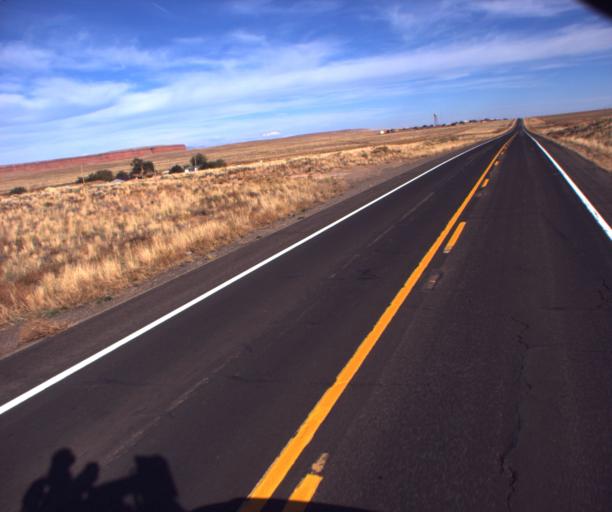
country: US
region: Arizona
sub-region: Apache County
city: Lukachukai
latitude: 36.9615
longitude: -109.4025
